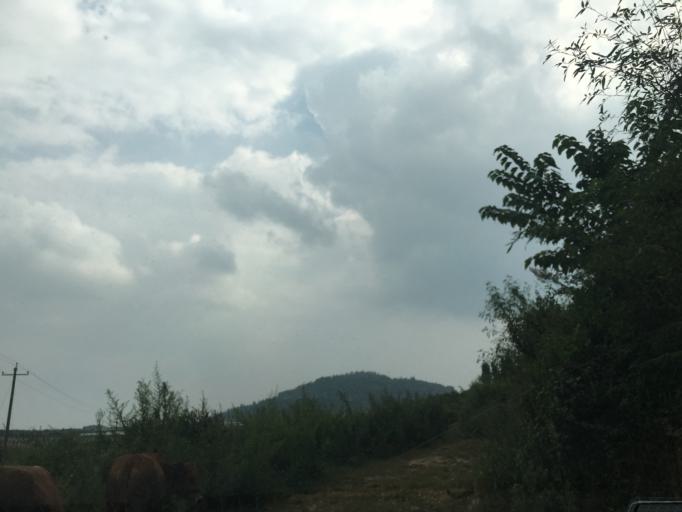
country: CN
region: Guangxi Zhuangzu Zizhiqu
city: Xinzhou
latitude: 25.4889
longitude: 105.6512
